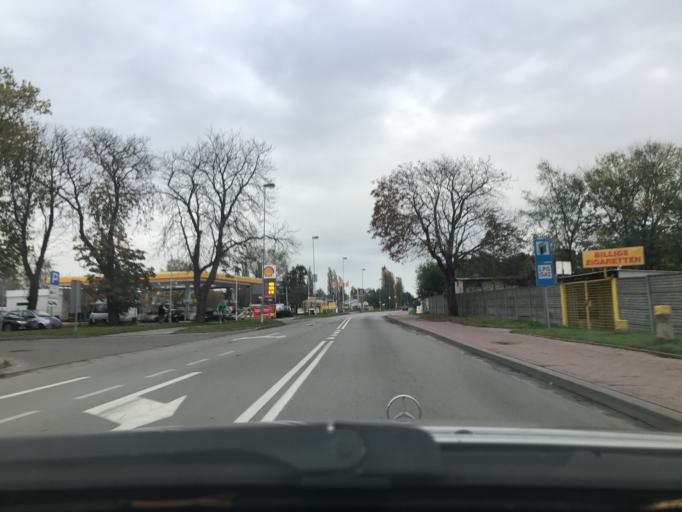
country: PL
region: West Pomeranian Voivodeship
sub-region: Swinoujscie
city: Swinoujscie
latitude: 53.8996
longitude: 14.2331
